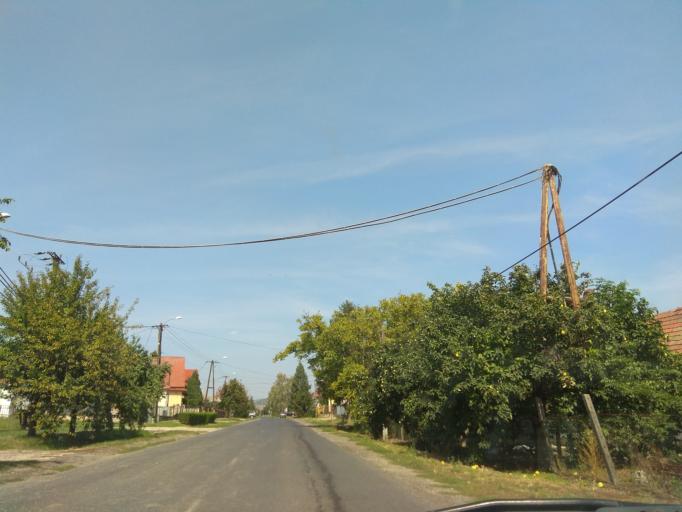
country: HU
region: Borsod-Abauj-Zemplen
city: Tallya
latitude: 48.2161
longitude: 21.2255
